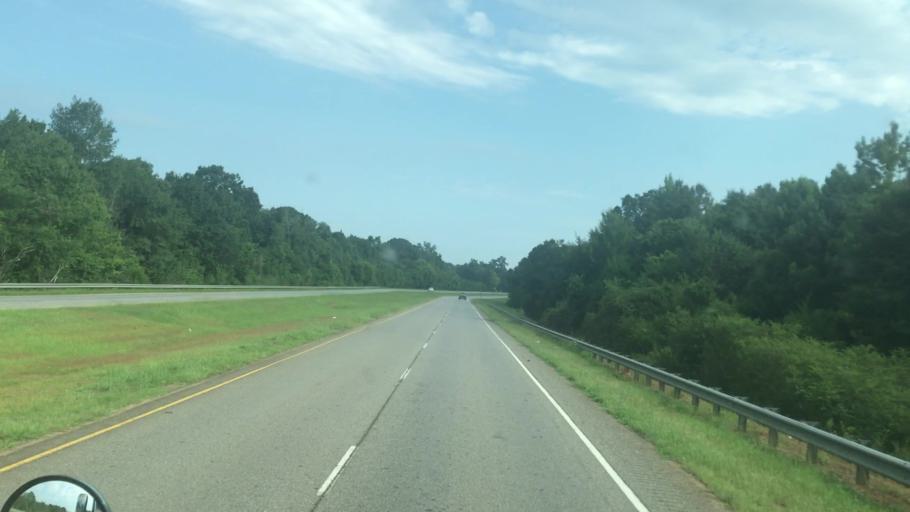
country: US
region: Georgia
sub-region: Early County
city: Blakely
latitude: 31.3684
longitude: -84.9203
